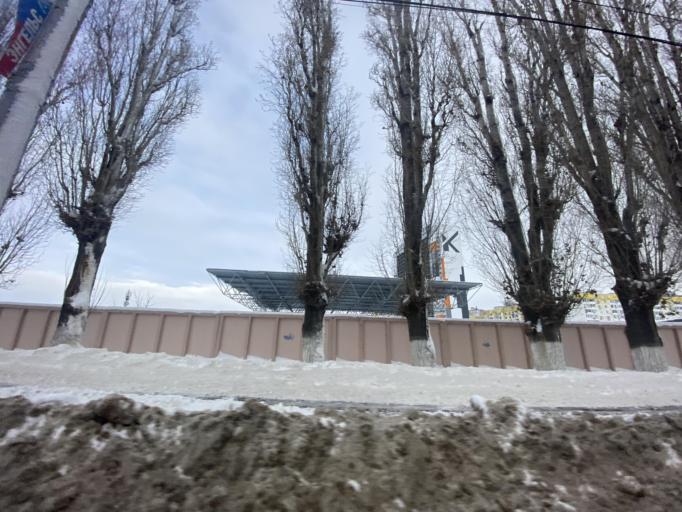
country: RU
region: Saratov
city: Engel's
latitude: 51.4994
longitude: 46.0864
